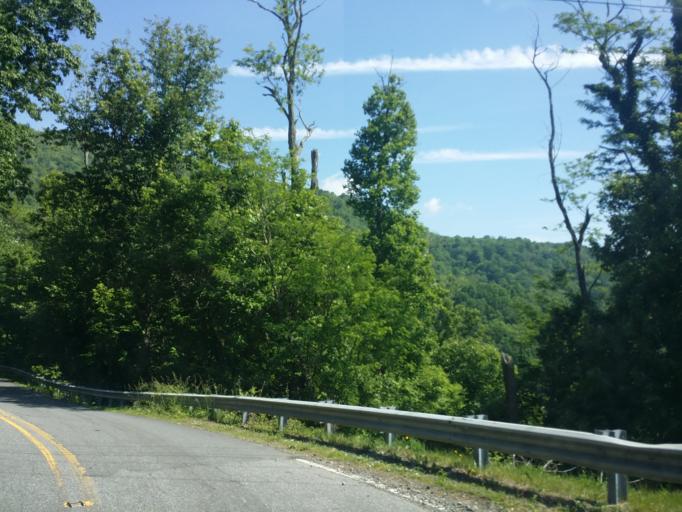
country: US
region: North Carolina
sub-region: Madison County
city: Marshall
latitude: 35.7048
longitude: -82.8245
